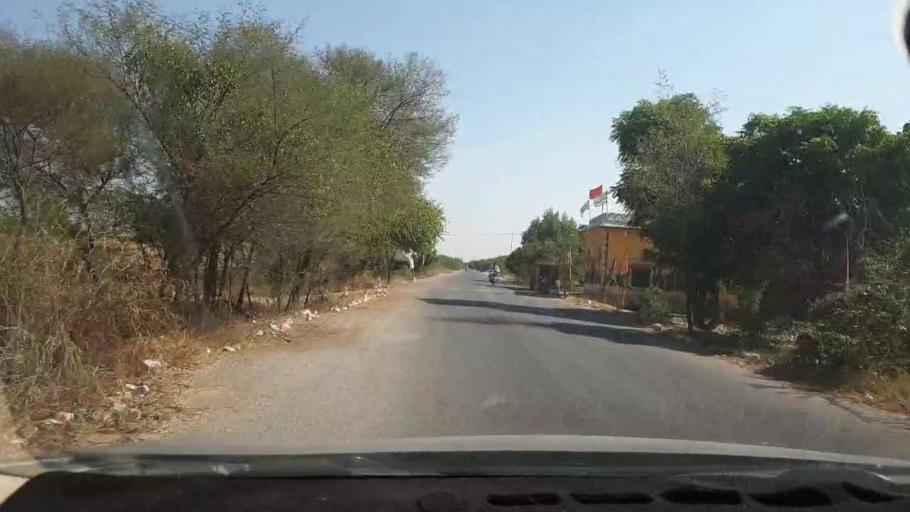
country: PK
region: Sindh
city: Malir Cantonment
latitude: 25.1414
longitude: 67.1998
